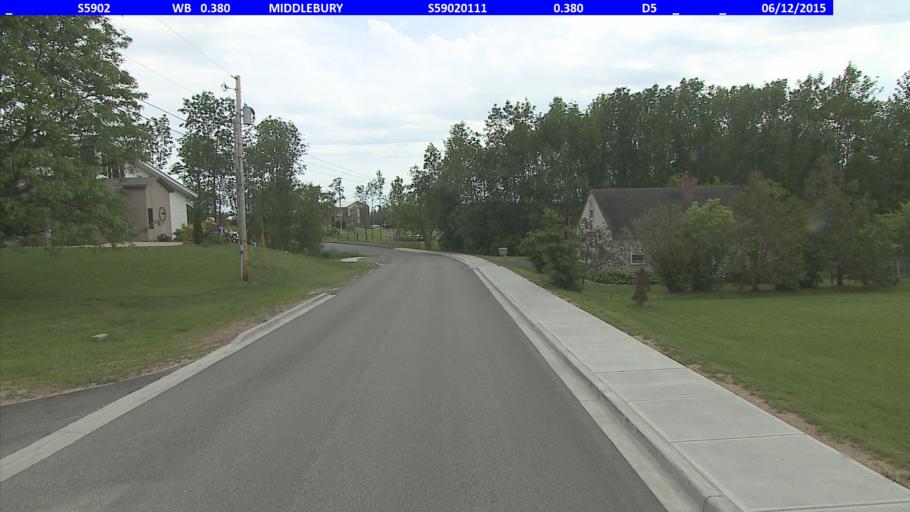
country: US
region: Vermont
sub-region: Addison County
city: Middlebury (village)
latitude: 44.0100
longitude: -73.1655
